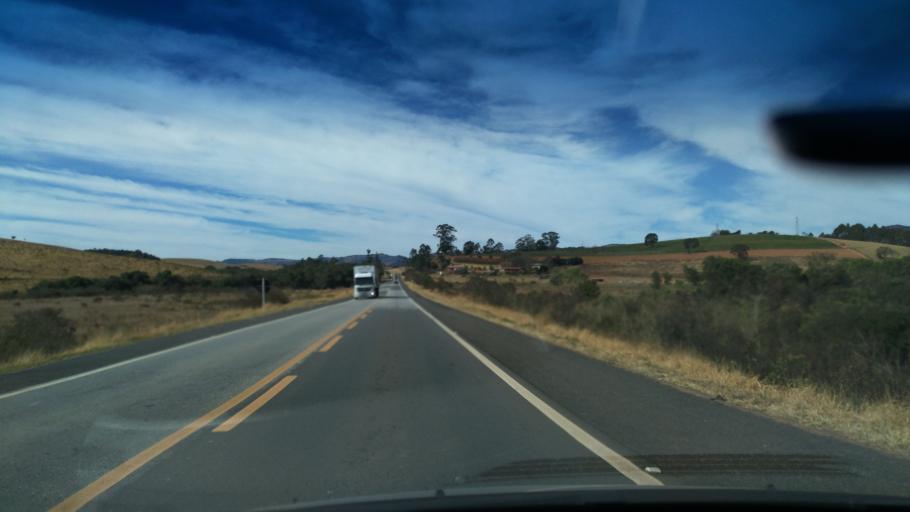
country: BR
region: Minas Gerais
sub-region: Borda Da Mata
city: Borda da Mata
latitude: -22.0566
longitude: -46.2863
